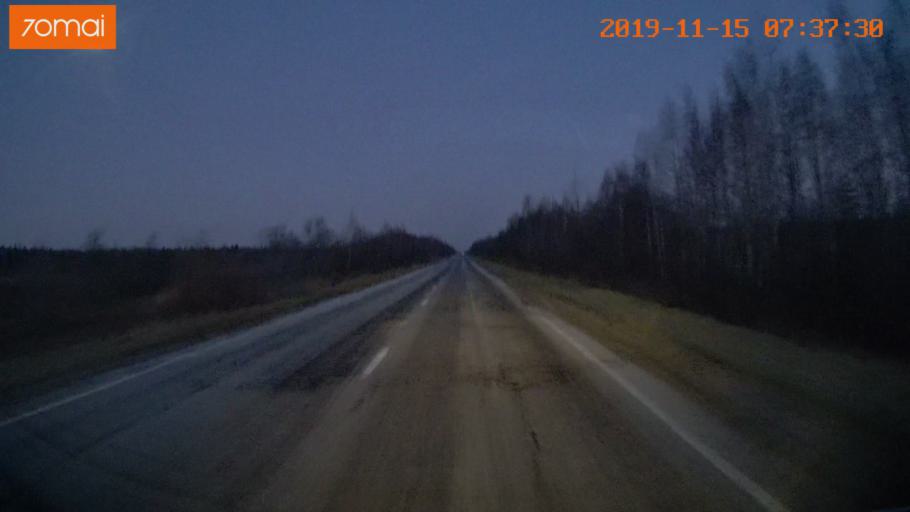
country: RU
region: Vologda
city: Sheksna
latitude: 58.7482
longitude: 38.4180
